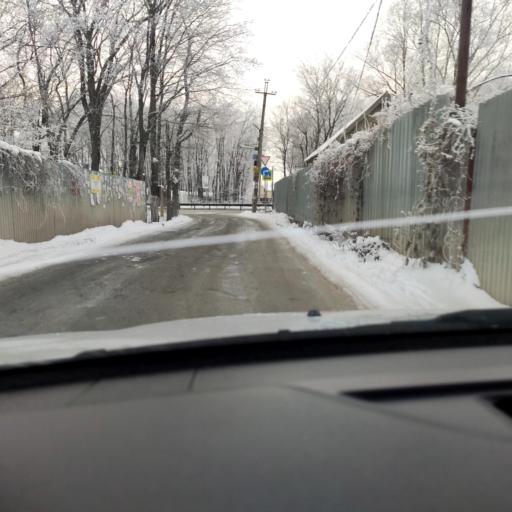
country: RU
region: Samara
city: Petra-Dubrava
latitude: 53.2963
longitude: 50.2461
